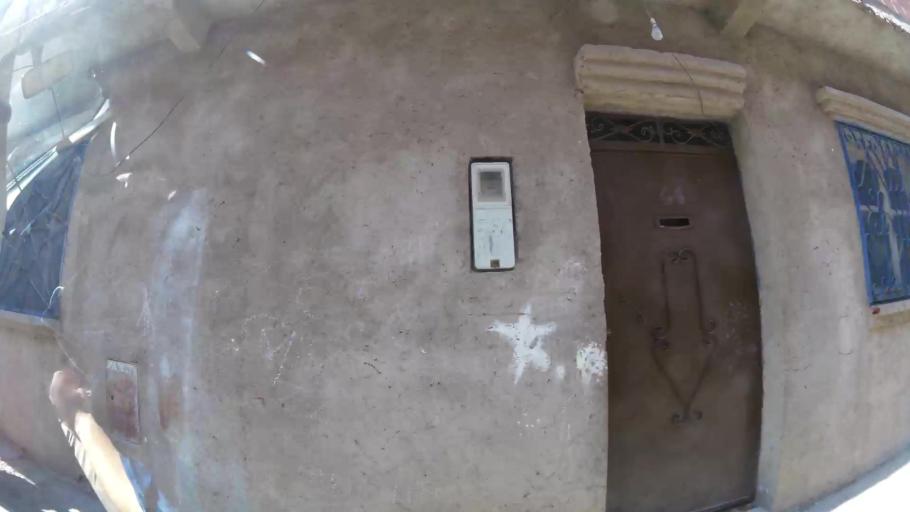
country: MA
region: Oriental
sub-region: Oujda-Angad
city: Oujda
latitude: 34.7206
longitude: -1.8856
